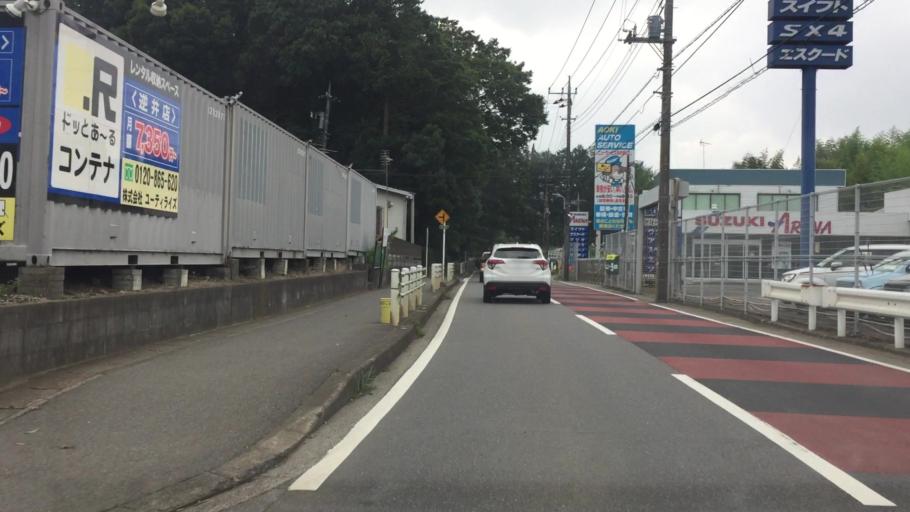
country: JP
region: Chiba
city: Kashiwa
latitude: 35.8153
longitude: 139.9816
